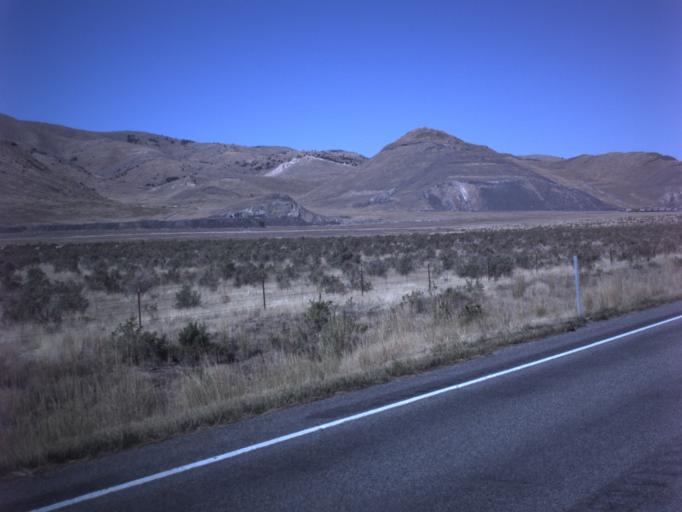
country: US
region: Utah
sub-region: Tooele County
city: Grantsville
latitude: 40.6623
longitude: -112.5405
